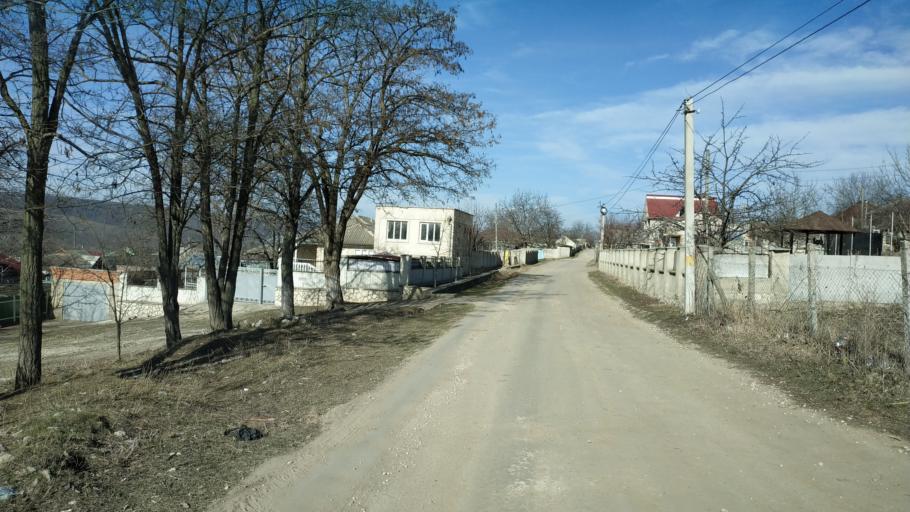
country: MD
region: Chisinau
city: Vatra
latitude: 47.0296
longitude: 28.6347
